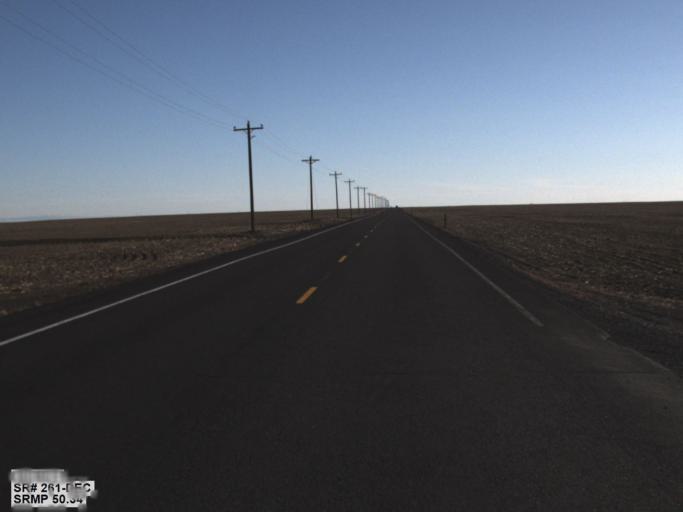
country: US
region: Washington
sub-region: Adams County
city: Ritzville
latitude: 46.9422
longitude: -118.3434
